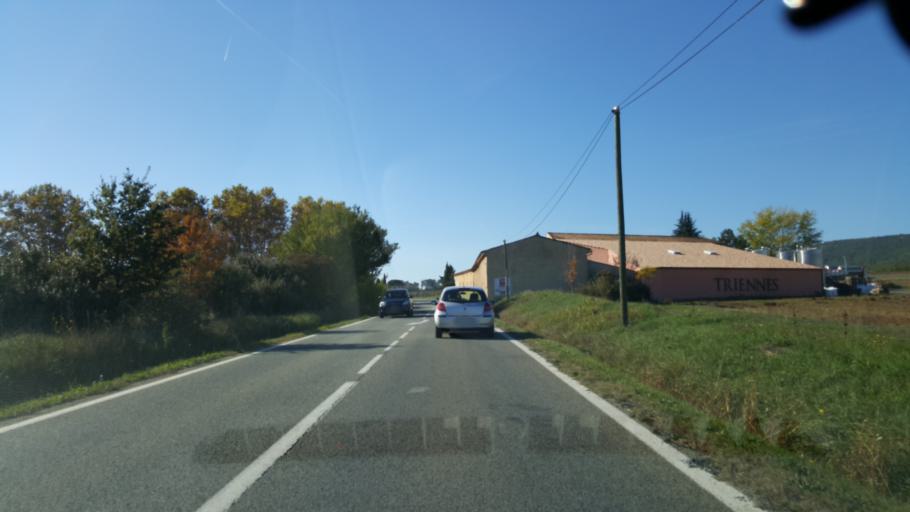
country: FR
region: Provence-Alpes-Cote d'Azur
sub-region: Departement du Var
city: Nans-les-Pins
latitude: 43.3924
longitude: 5.7913
